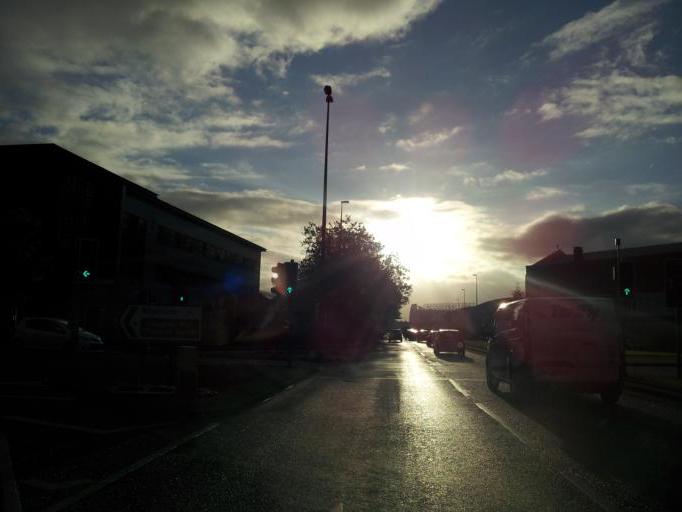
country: GB
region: England
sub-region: Trafford
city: Trafford Park
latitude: 53.4675
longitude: -2.3050
